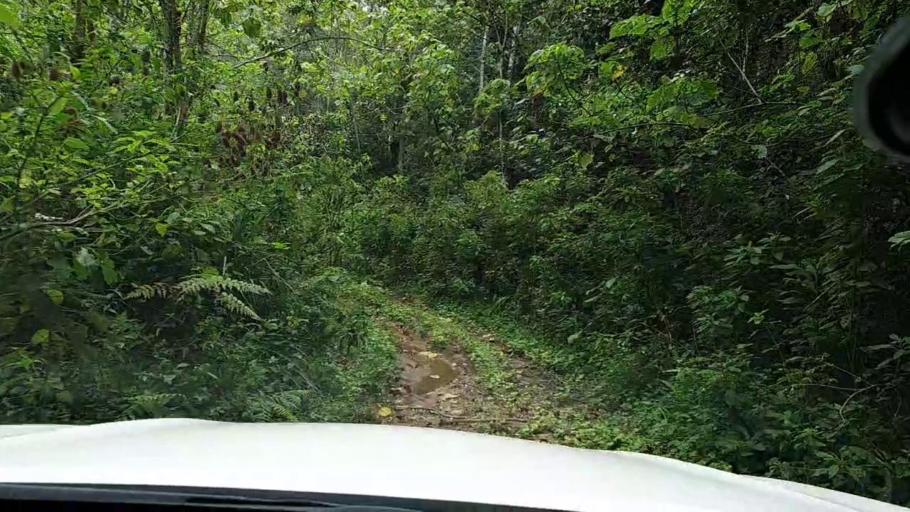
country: RW
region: Western Province
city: Kibuye
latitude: -2.2876
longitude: 29.3049
